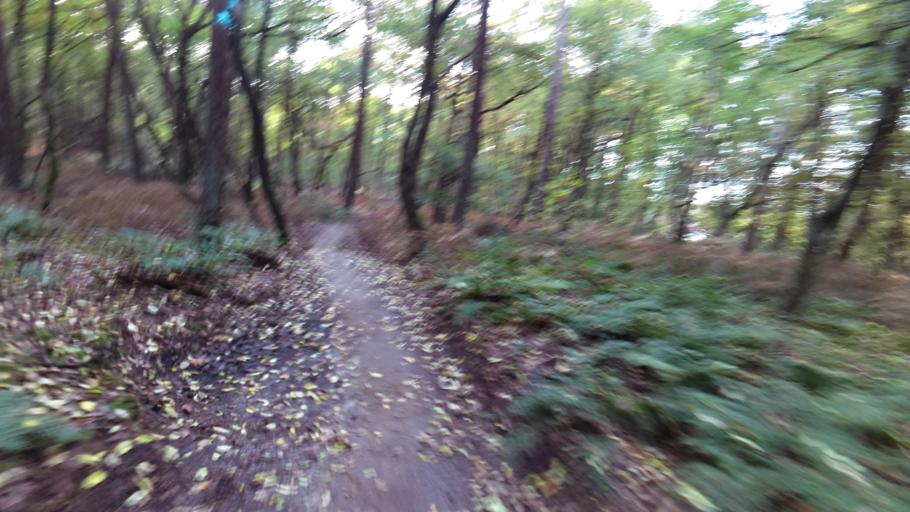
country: NL
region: Gelderland
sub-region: Gemeente Ede
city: Ede
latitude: 52.0652
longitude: 5.6659
